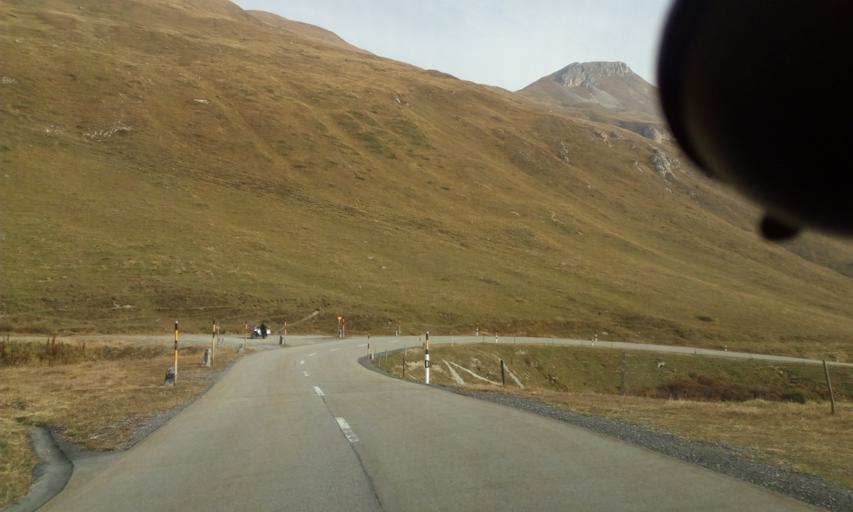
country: CH
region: Grisons
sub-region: Maloja District
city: Ponte
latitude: 46.5884
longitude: 9.8841
